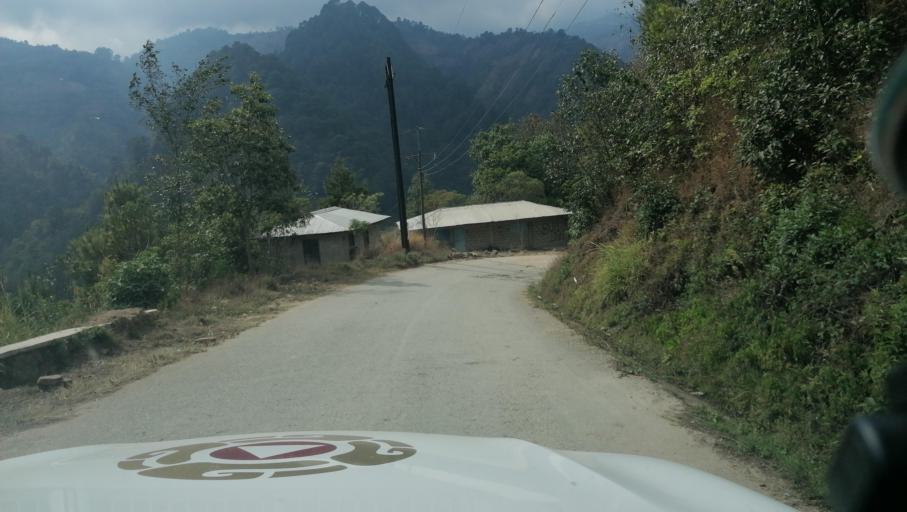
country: GT
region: San Marcos
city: Tacana
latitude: 15.2117
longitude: -92.1970
